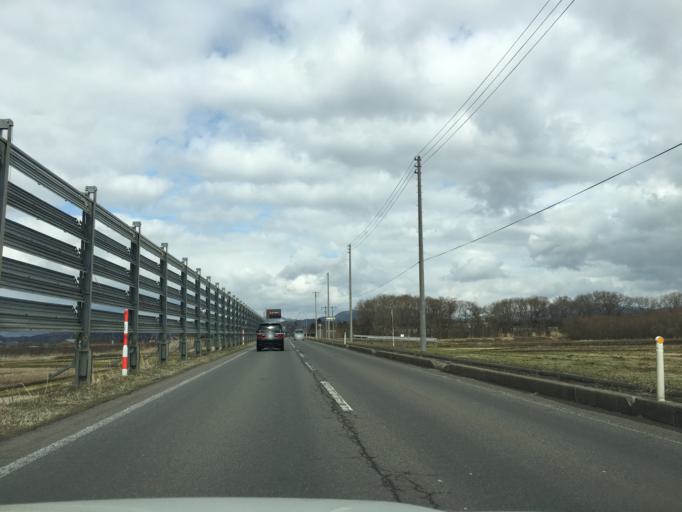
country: JP
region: Akita
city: Hanawa
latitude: 40.2517
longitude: 140.7586
